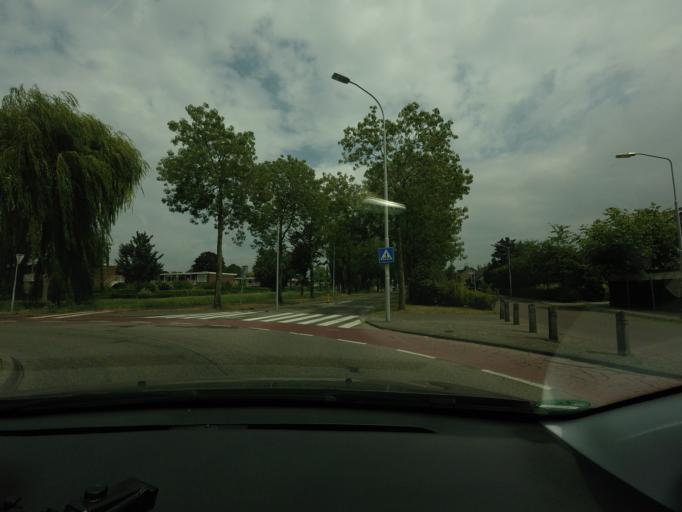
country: NL
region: Gelderland
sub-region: Gemeente Tiel
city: Tiel
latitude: 51.8802
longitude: 5.4211
